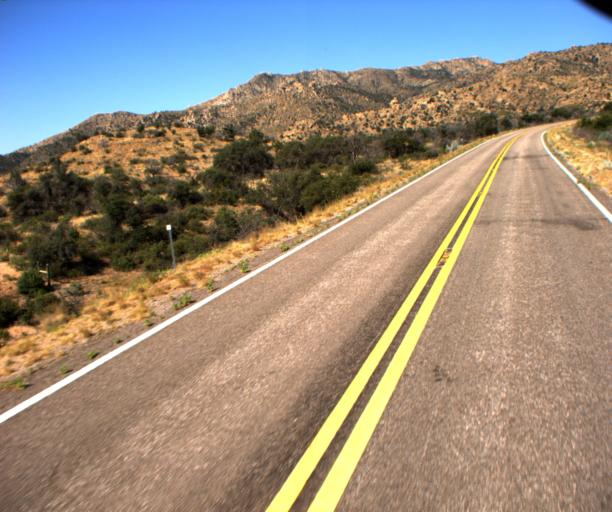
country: US
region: Arizona
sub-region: Graham County
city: Swift Trail Junction
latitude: 32.5707
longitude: -109.8221
